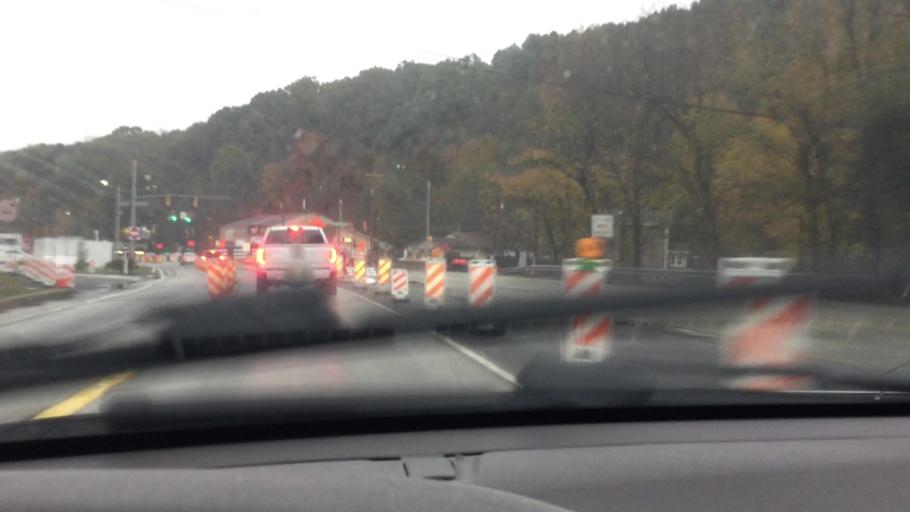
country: US
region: Pennsylvania
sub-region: Allegheny County
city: Elizabeth
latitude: 40.2637
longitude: -79.8784
